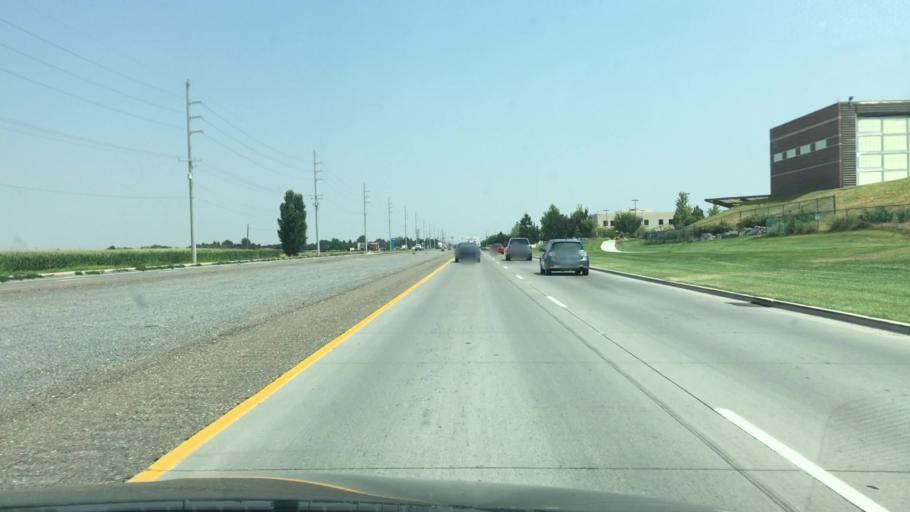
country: US
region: Idaho
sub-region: Twin Falls County
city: Twin Falls
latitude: 42.5916
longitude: -114.4971
